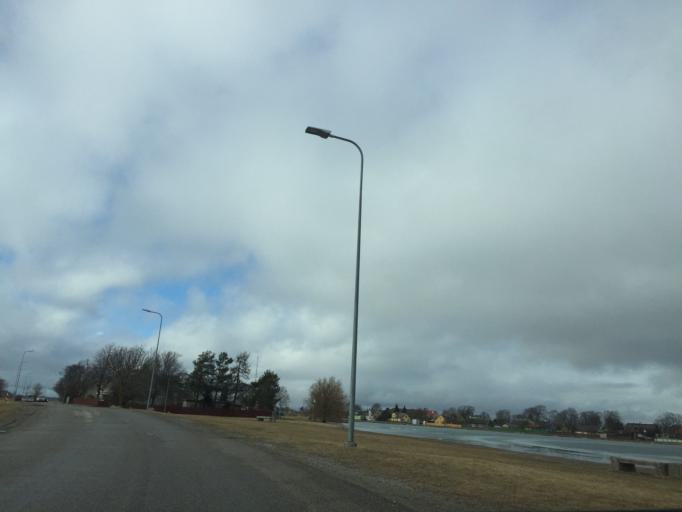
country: EE
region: Laeaene
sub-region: Haapsalu linn
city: Haapsalu
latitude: 58.9516
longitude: 23.5263
